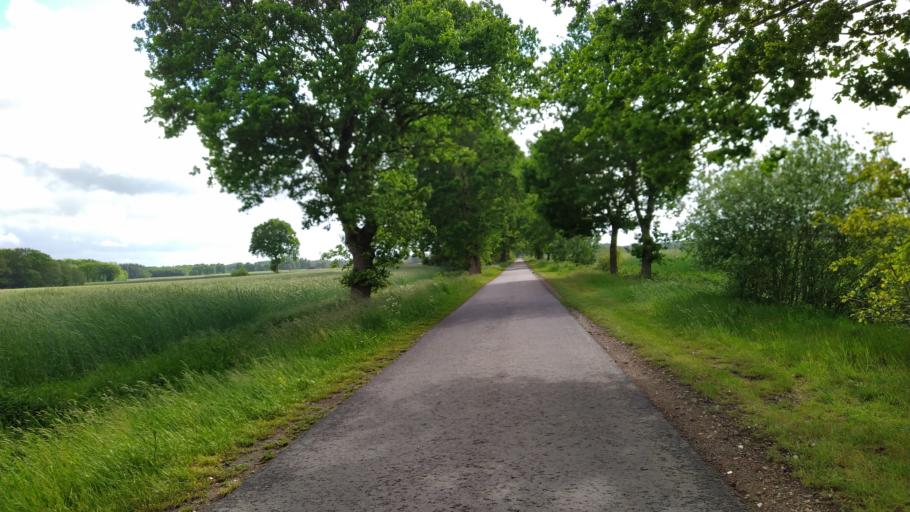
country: DE
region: Lower Saxony
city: Brest
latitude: 53.4465
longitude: 9.3729
